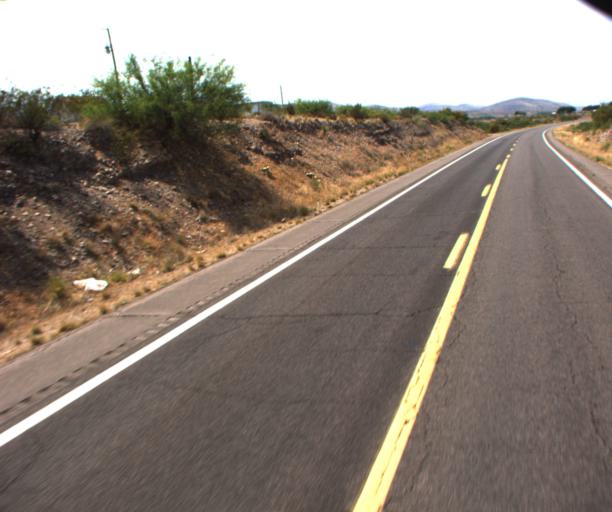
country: US
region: Arizona
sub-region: Greenlee County
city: Clifton
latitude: 32.8143
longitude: -109.1702
